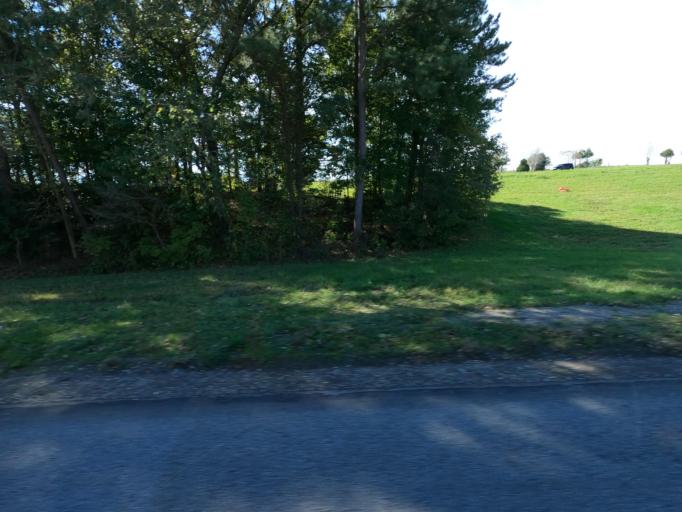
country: US
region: Tennessee
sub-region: Dickson County
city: Burns
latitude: 36.0237
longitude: -87.2709
